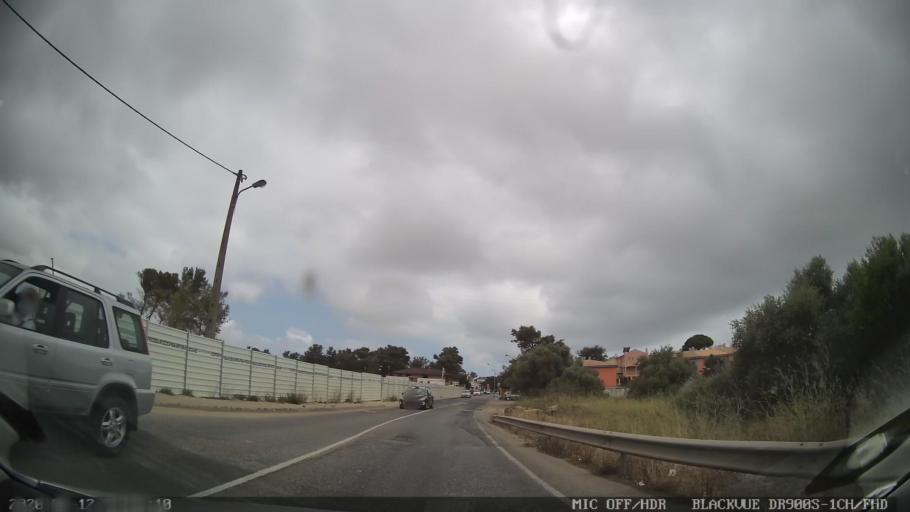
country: PT
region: Lisbon
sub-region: Cascais
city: Estoril
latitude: 38.7144
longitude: -9.3877
